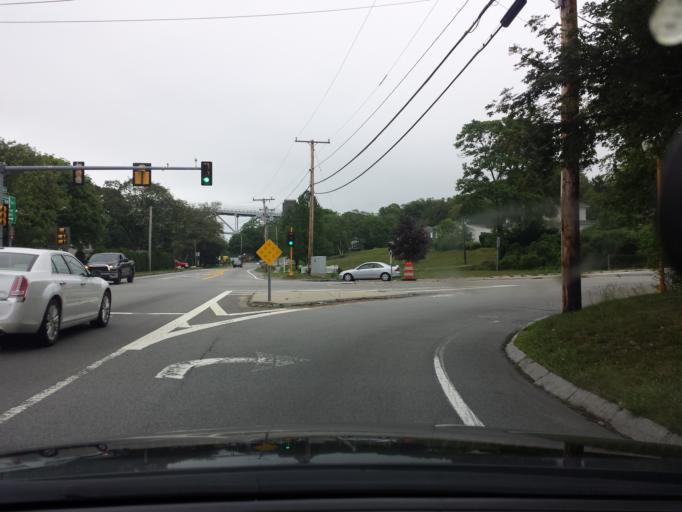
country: US
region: Massachusetts
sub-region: Barnstable County
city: Sagamore
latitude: 41.7742
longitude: -70.5480
